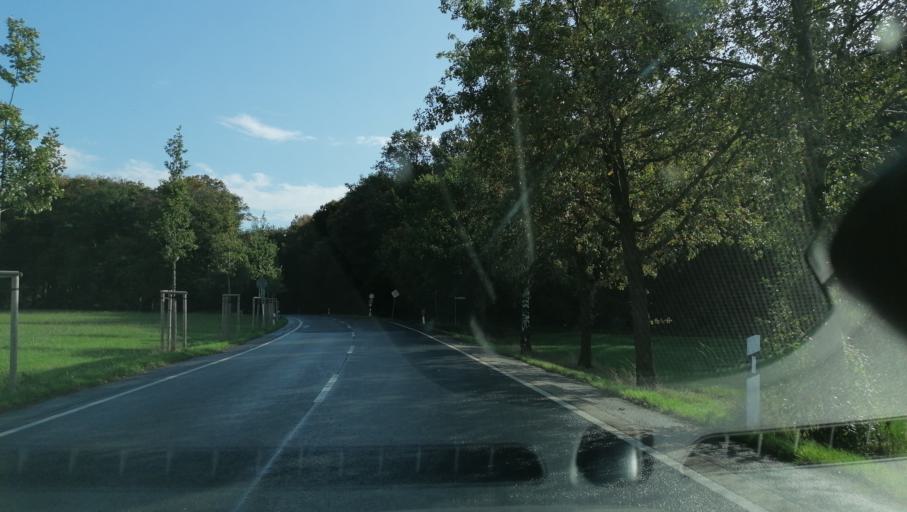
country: DE
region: North Rhine-Westphalia
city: Waltrop
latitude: 51.6265
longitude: 7.3515
